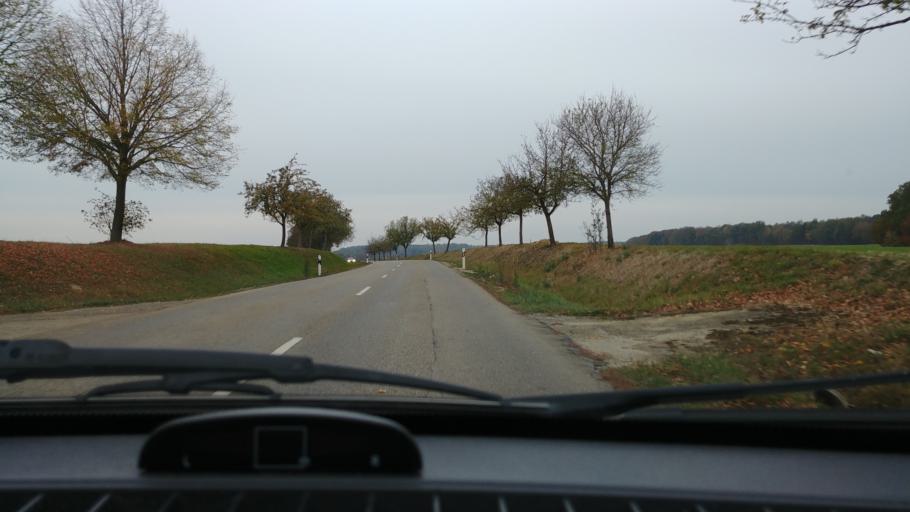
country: DE
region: Baden-Wuerttemberg
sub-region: Regierungsbezirk Stuttgart
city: Schrozberg
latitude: 49.3404
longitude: 10.0491
